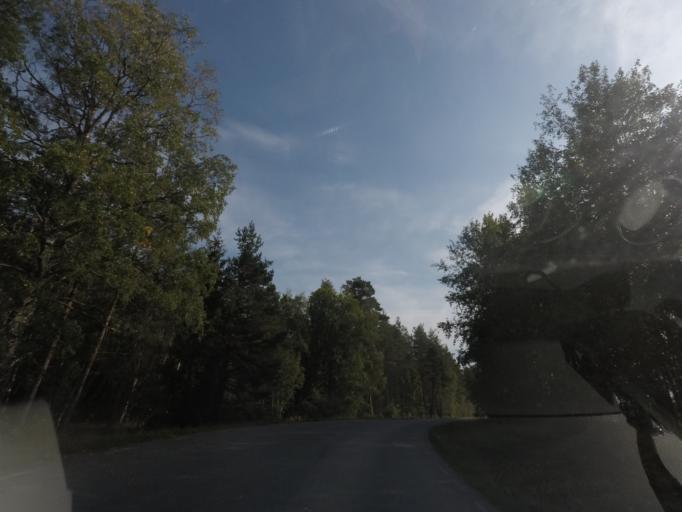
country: SE
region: Vaestmanland
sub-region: Kungsors Kommun
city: Kungsoer
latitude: 59.5149
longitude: 16.1486
